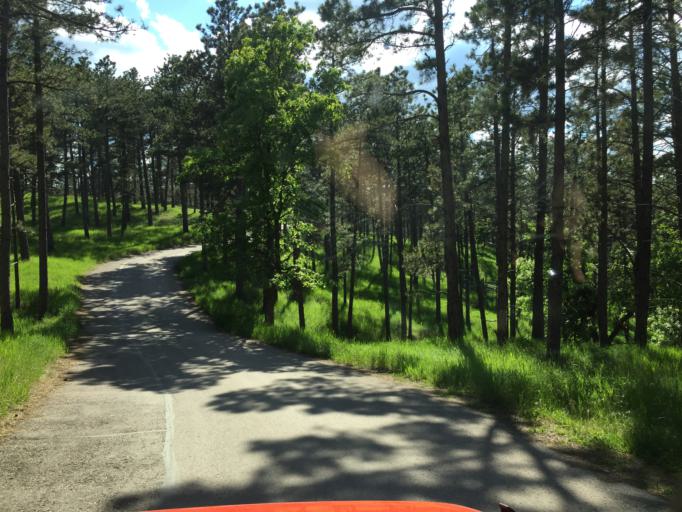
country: US
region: South Dakota
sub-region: Pennington County
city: Colonial Pine Hills
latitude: 43.9784
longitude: -103.3013
